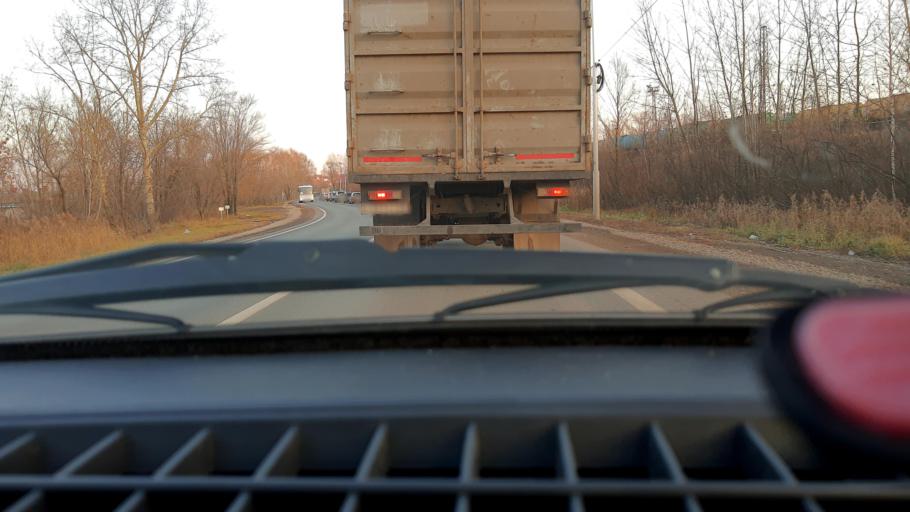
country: RU
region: Bashkortostan
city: Ufa
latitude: 54.8396
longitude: 56.1251
